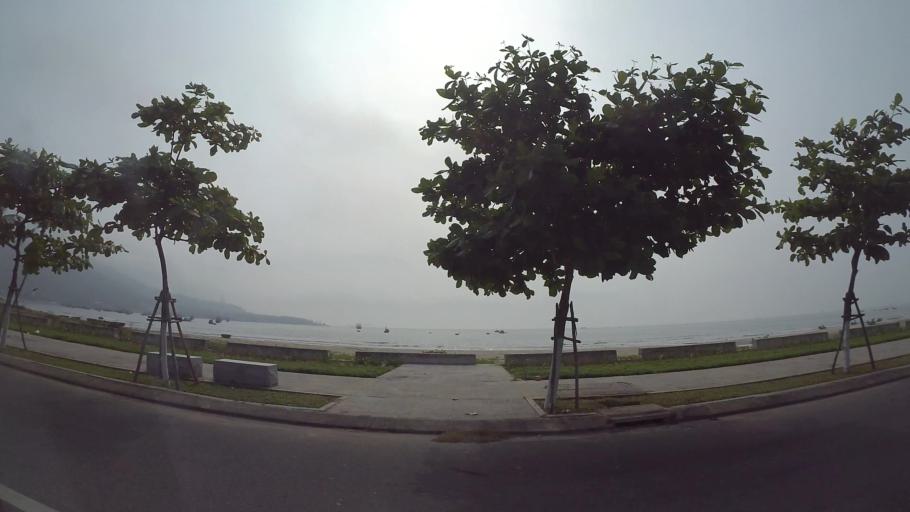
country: VN
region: Da Nang
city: Son Tra
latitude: 16.0969
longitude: 108.2529
